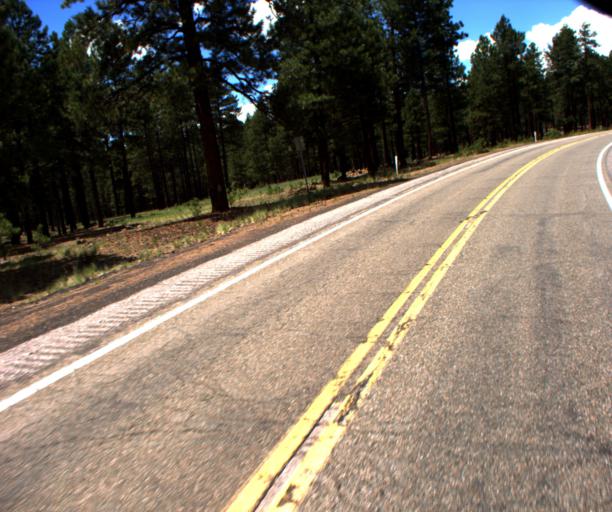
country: US
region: Arizona
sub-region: Coconino County
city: Flagstaff
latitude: 35.2810
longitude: -111.7487
